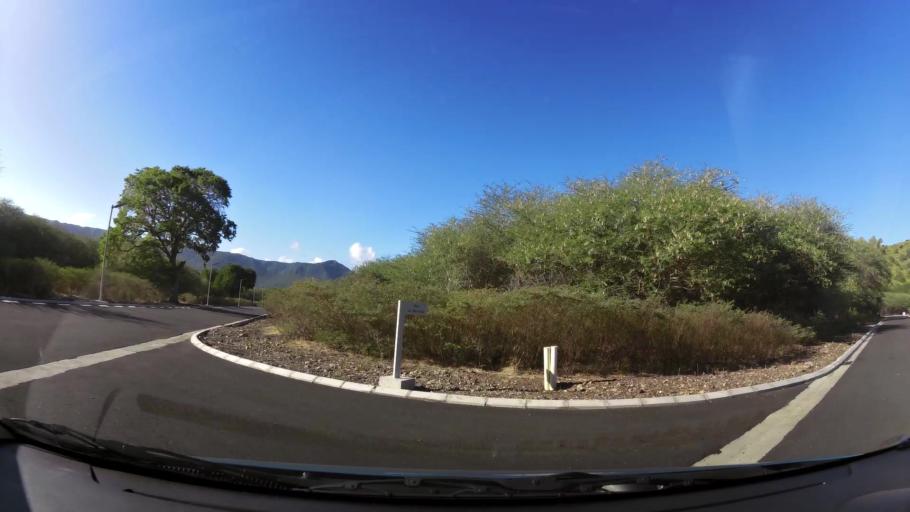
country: MU
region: Black River
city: Tamarin
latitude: -20.3442
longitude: 57.3919
